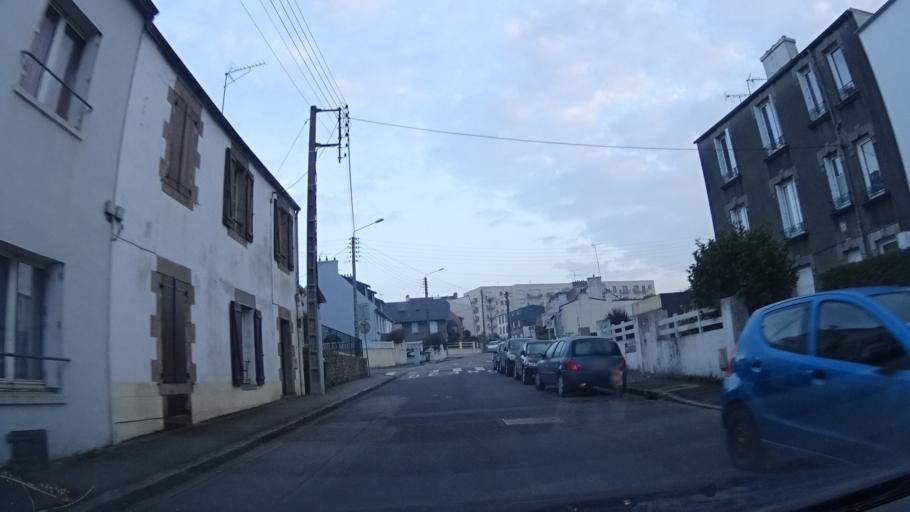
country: FR
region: Brittany
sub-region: Departement du Finistere
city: Brest
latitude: 48.3965
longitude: -4.4583
